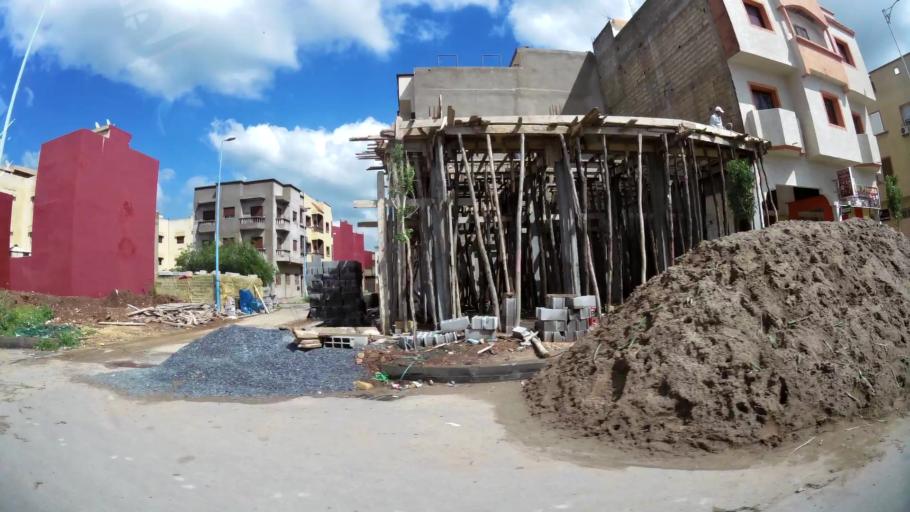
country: MA
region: Grand Casablanca
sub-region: Mediouna
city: Mediouna
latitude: 33.3772
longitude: -7.5361
